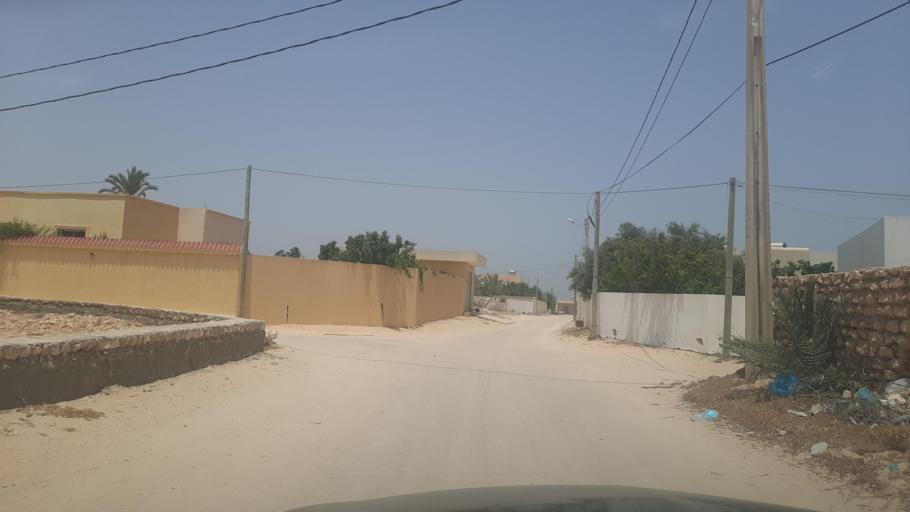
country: TN
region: Safaqis
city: Al Qarmadah
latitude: 34.6510
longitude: 11.0261
